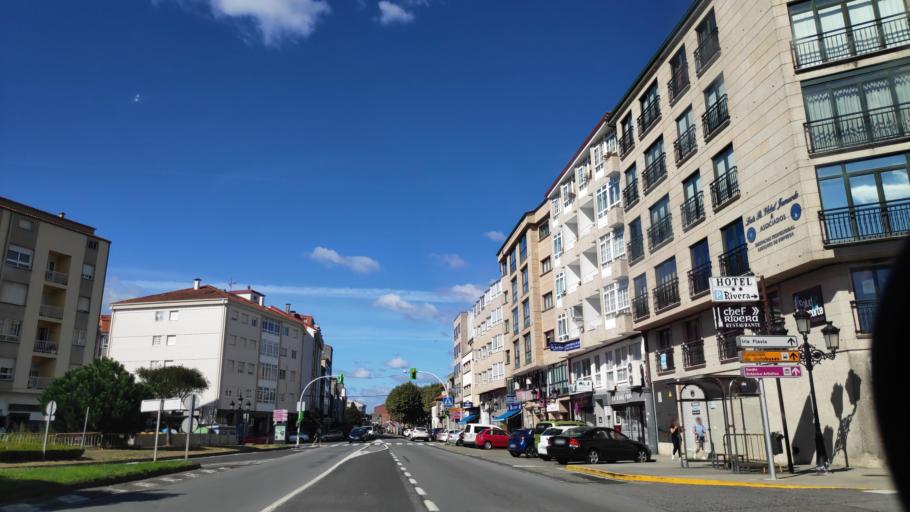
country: ES
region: Galicia
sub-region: Provincia da Coruna
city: Padron
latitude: 42.7366
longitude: -8.6598
